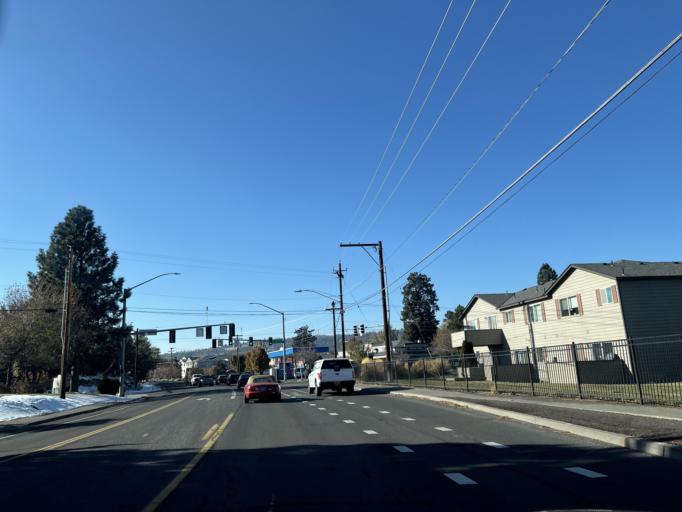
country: US
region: Oregon
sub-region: Deschutes County
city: Bend
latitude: 44.0765
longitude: -121.2945
